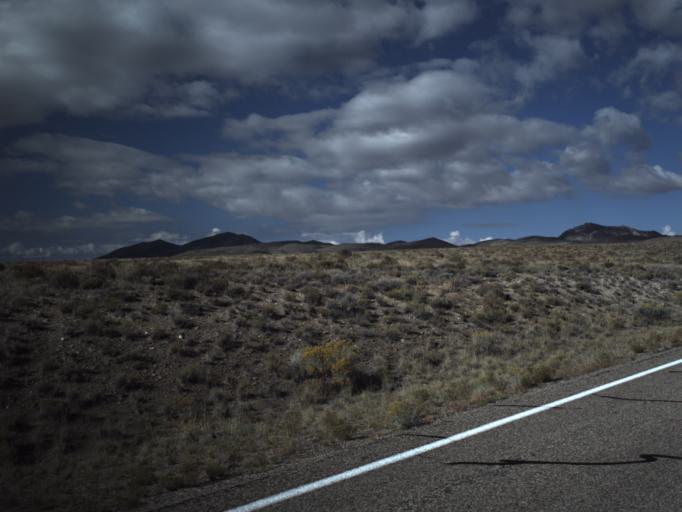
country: US
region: Utah
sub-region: Beaver County
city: Milford
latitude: 38.4489
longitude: -113.1931
